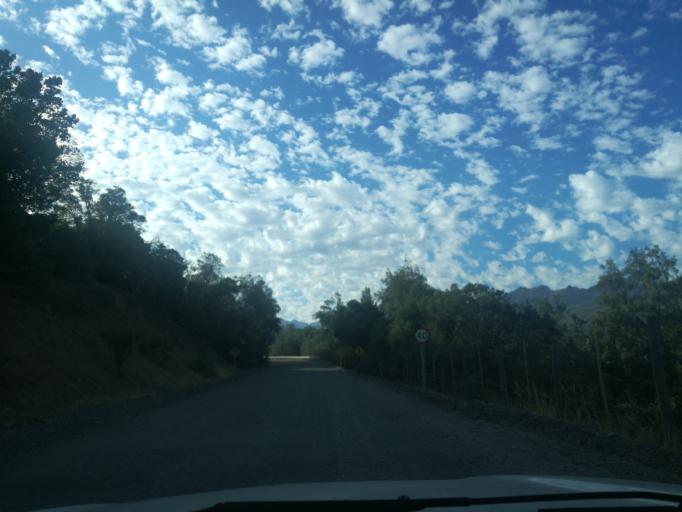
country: CL
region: O'Higgins
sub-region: Provincia de Cachapoal
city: Machali
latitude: -34.2528
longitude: -70.4663
